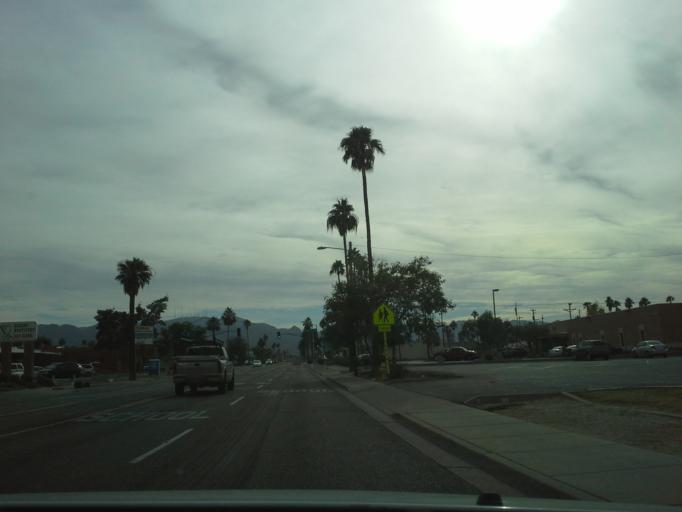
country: US
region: Arizona
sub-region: Maricopa County
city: Phoenix
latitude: 33.3898
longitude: -112.0734
